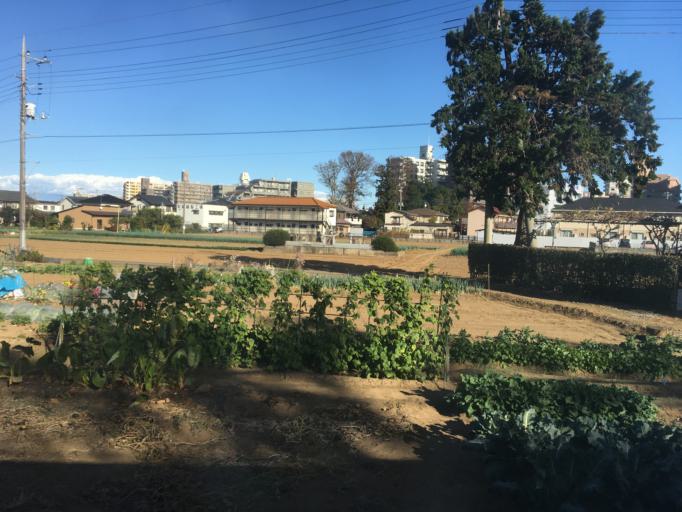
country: JP
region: Saitama
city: Sakado
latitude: 35.9591
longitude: 139.3891
